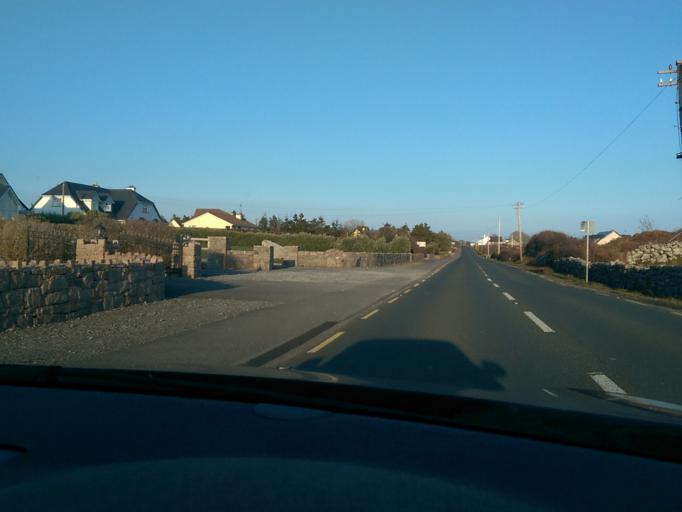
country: IE
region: Connaught
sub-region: County Galway
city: Oughterard
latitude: 53.2440
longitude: -9.3314
